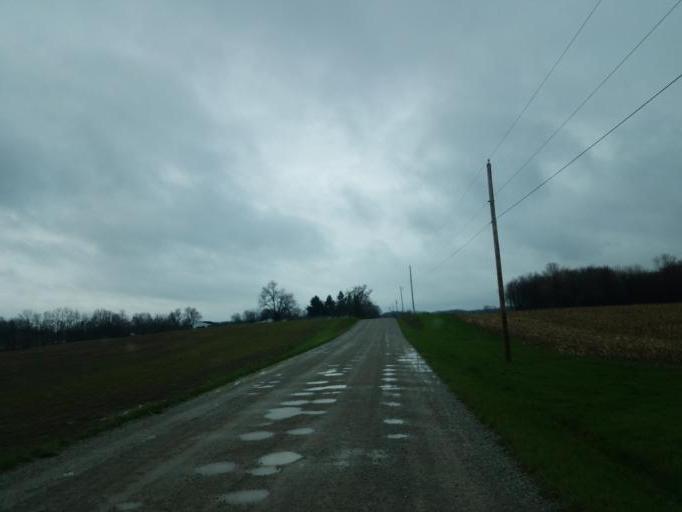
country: US
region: Ohio
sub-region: Morrow County
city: Mount Gilead
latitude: 40.4827
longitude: -82.7225
